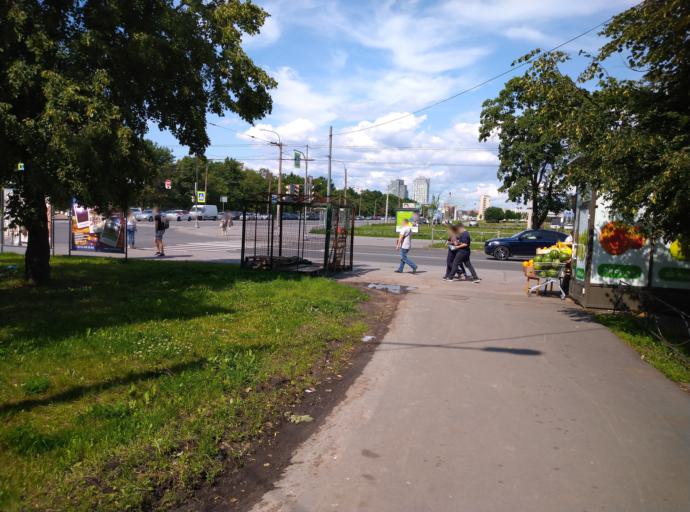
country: RU
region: St.-Petersburg
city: Kupchino
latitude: 59.8642
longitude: 30.3377
